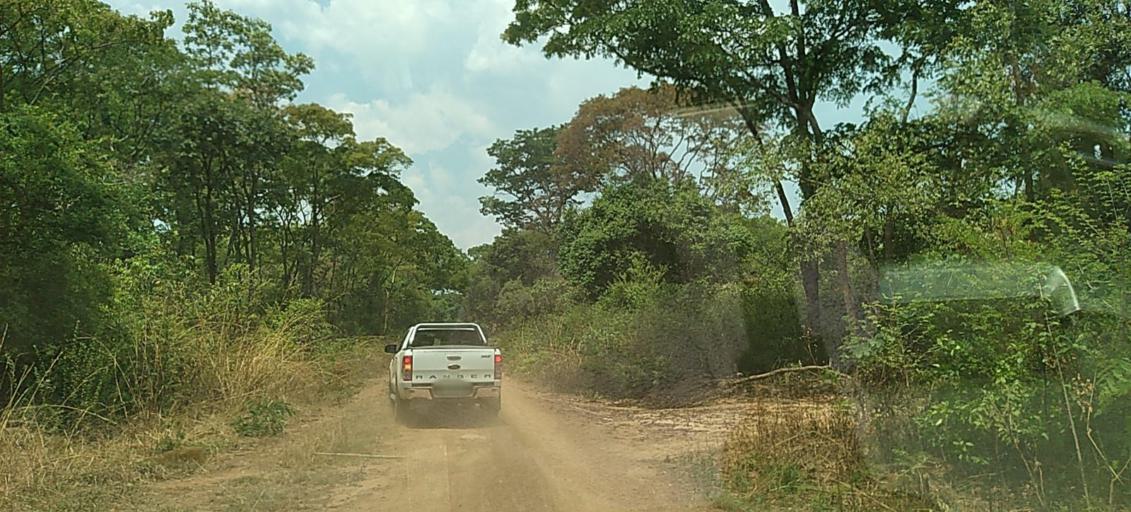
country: ZM
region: Copperbelt
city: Chingola
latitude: -12.7901
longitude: 27.6498
